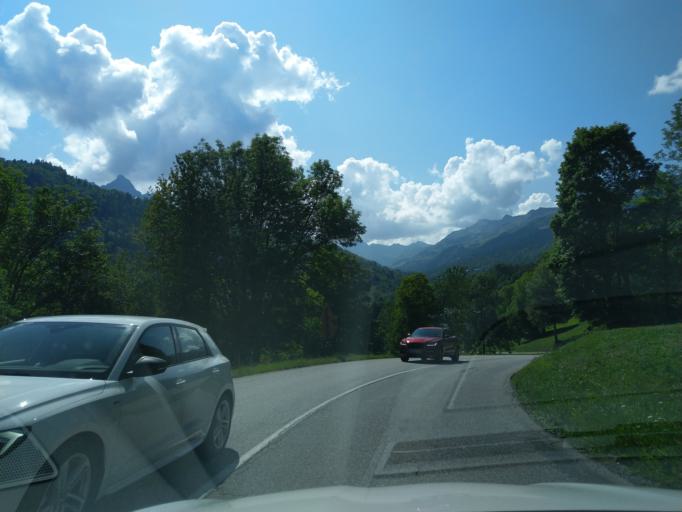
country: FR
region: Rhone-Alpes
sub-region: Departement de la Savoie
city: Les Allues
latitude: 45.4250
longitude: 6.5549
